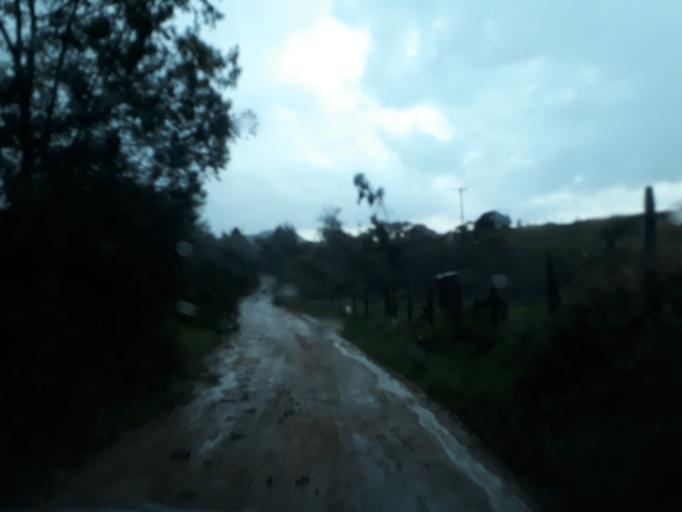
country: CO
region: Cundinamarca
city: Villapinzon
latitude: 5.2985
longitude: -73.6041
